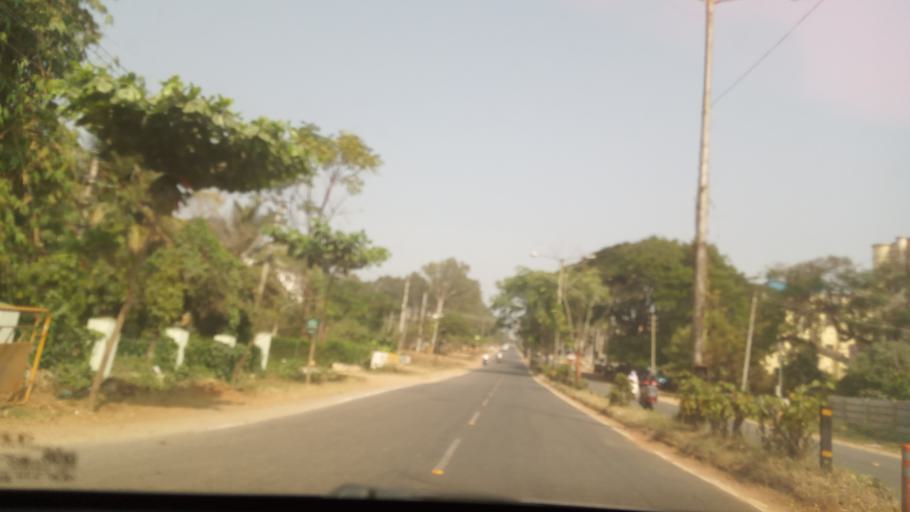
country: IN
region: Karnataka
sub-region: Mysore
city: Mysore
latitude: 12.3374
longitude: 76.6319
